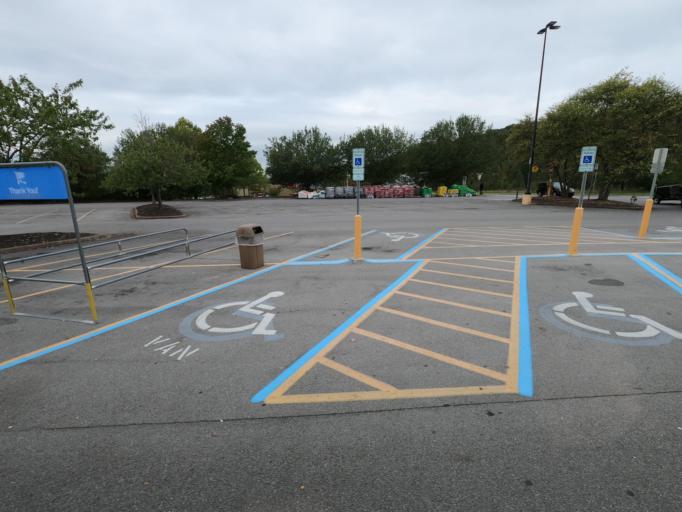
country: US
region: Tennessee
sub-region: Sullivan County
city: Kingsport
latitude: 36.5565
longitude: -82.6041
